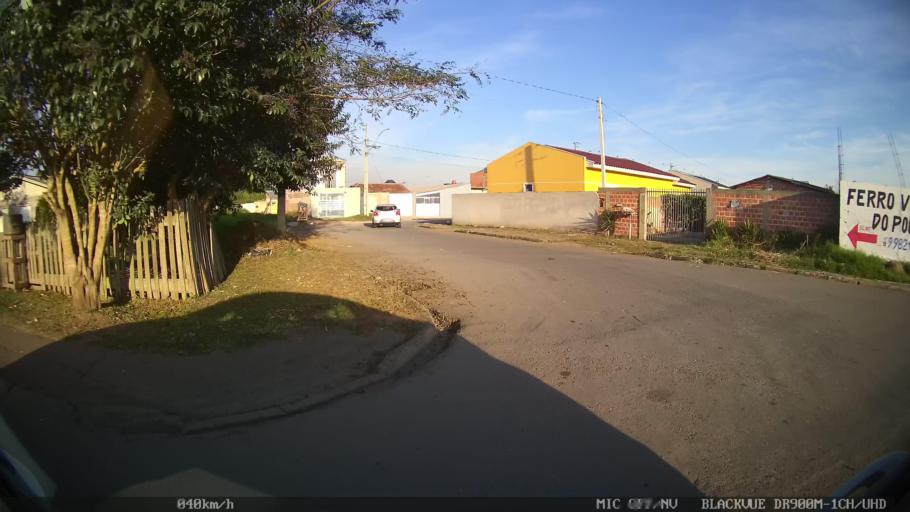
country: BR
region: Parana
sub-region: Pinhais
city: Pinhais
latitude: -25.4466
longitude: -49.1401
